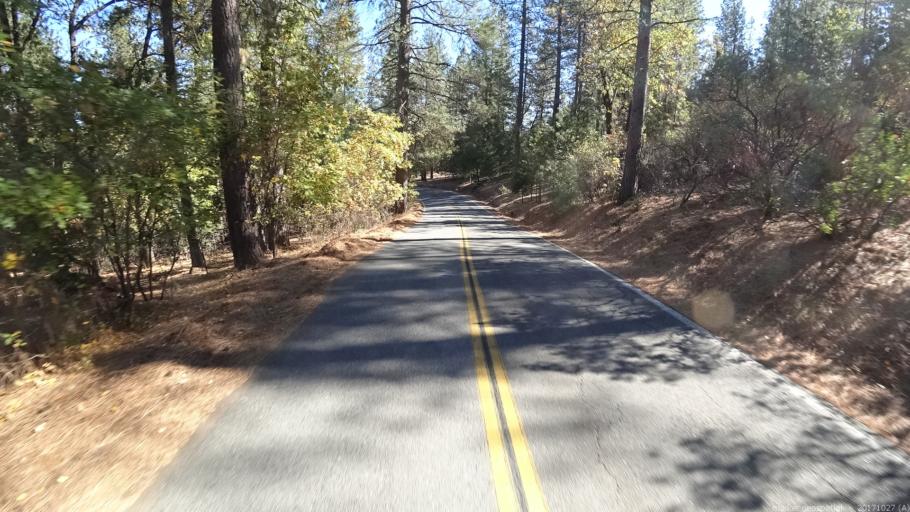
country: US
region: California
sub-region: Shasta County
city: Bella Vista
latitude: 40.7285
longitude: -122.0169
